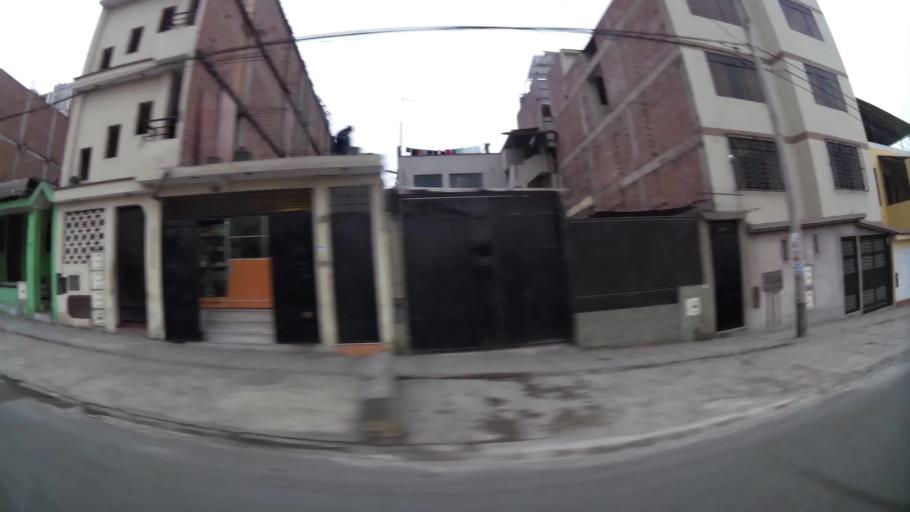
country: PE
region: Lima
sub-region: Lima
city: Vitarte
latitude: -12.0119
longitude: -76.9794
